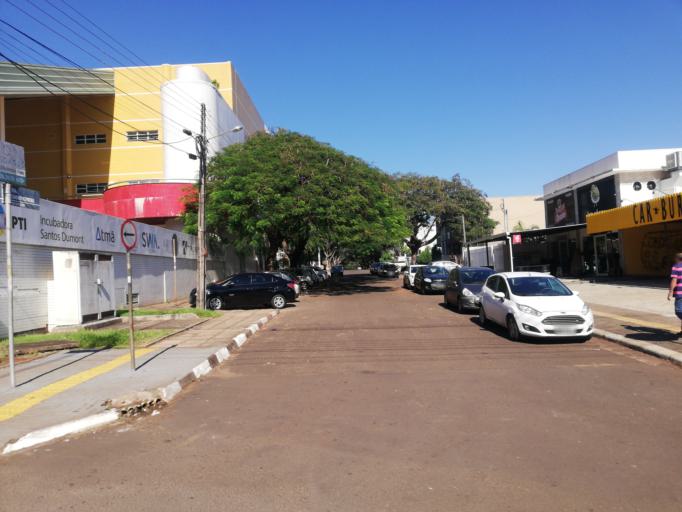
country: BR
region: Parana
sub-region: Foz Do Iguacu
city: Foz do Iguacu
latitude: -25.5528
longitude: -54.5700
